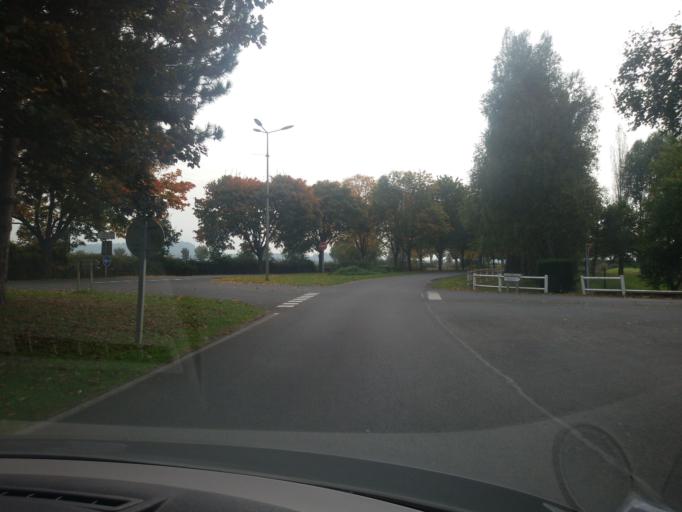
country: FR
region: Lower Normandy
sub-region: Departement du Calvados
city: Cabourg
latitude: 49.2763
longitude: -0.1170
